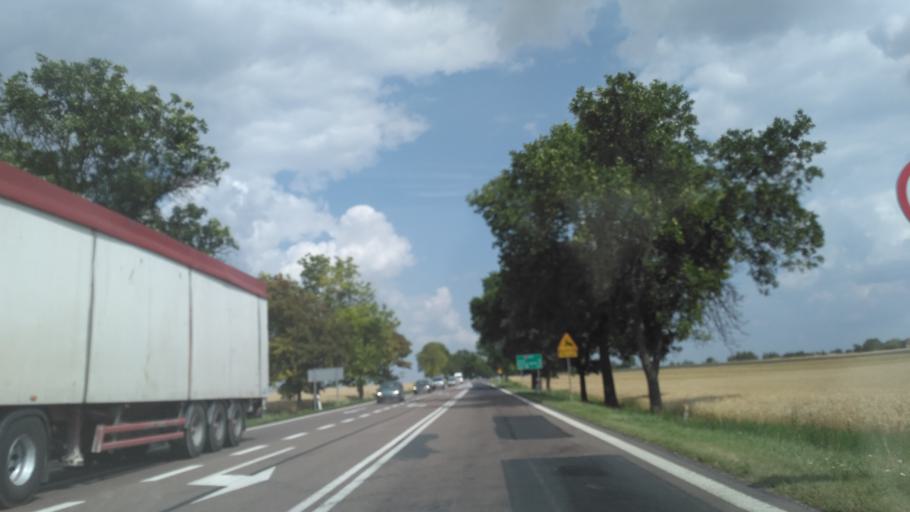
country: PL
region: Lublin Voivodeship
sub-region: Powiat chelmski
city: Rejowiec Fabryczny
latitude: 51.1781
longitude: 23.2028
